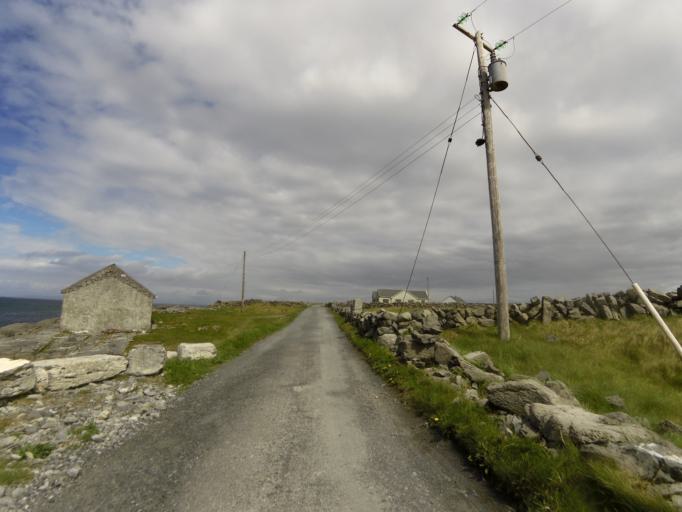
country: IE
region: Connaught
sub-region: County Galway
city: Clifden
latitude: 53.1316
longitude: -9.7471
